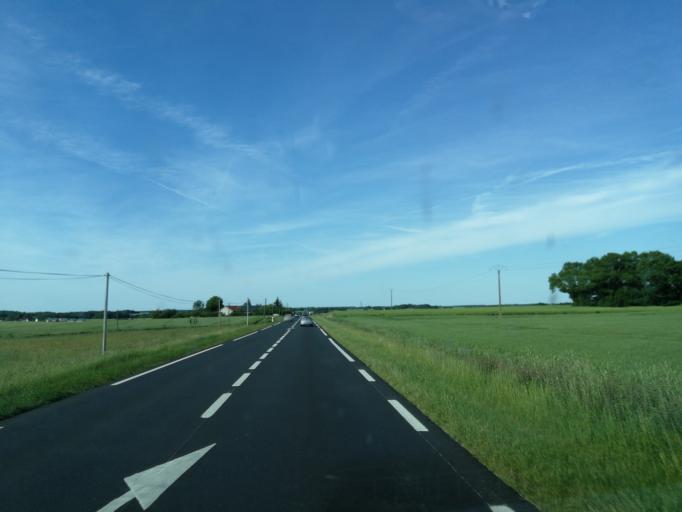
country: FR
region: Centre
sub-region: Departement d'Indre-et-Loire
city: Chateau-Renault
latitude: 47.6352
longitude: 0.9425
